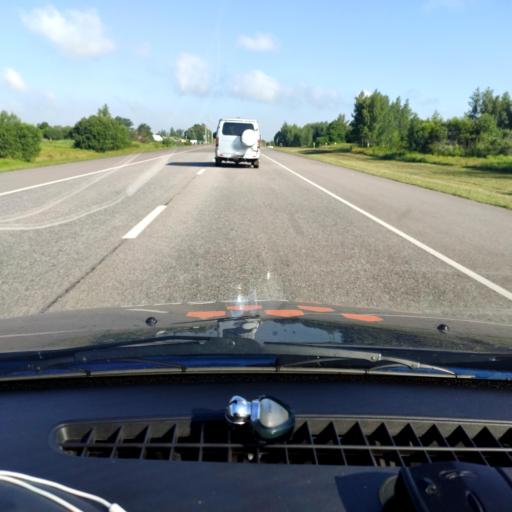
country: RU
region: Orjol
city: Orel
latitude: 52.8739
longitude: 36.1793
